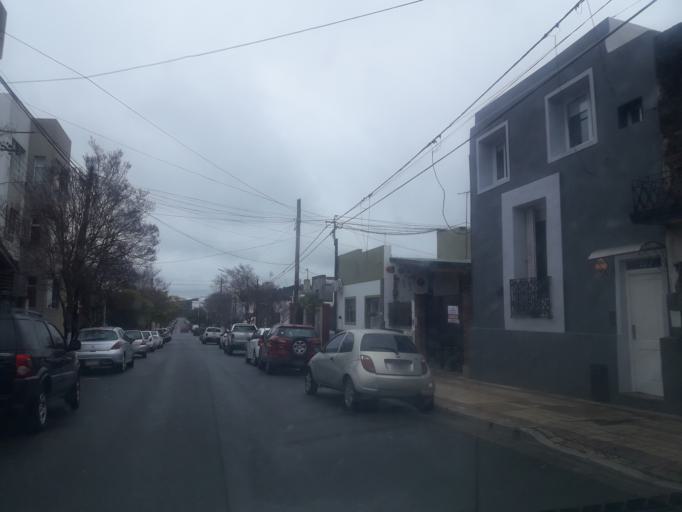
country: AR
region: Buenos Aires
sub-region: Partido de Tandil
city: Tandil
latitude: -37.3329
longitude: -59.1381
